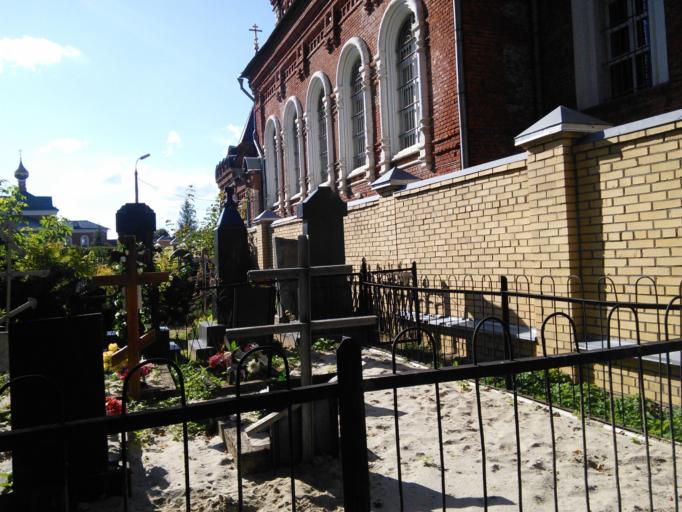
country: RU
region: Moskovskaya
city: Pavlovskiy Posad
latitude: 55.7890
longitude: 38.6524
